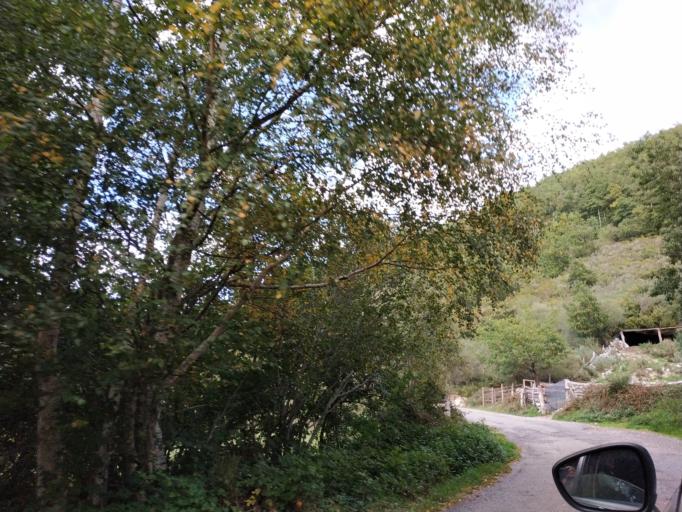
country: ES
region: Castille and Leon
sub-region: Provincia de Leon
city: Candin
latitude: 42.8603
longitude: -6.8544
